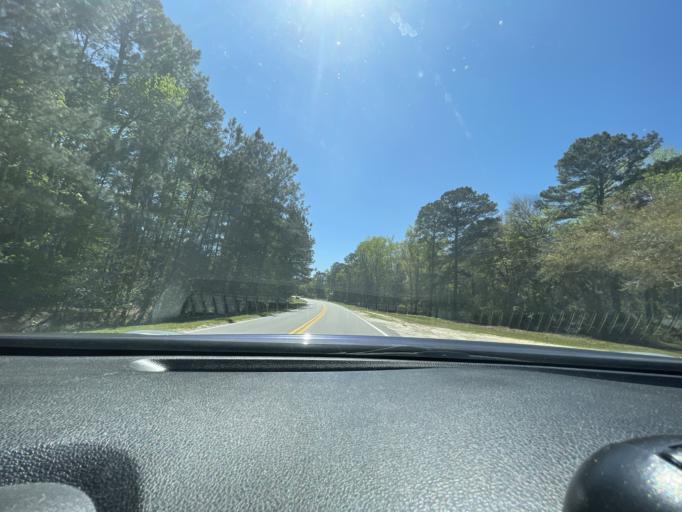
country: US
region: Georgia
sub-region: Chatham County
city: Pooler
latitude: 32.0945
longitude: -81.2391
